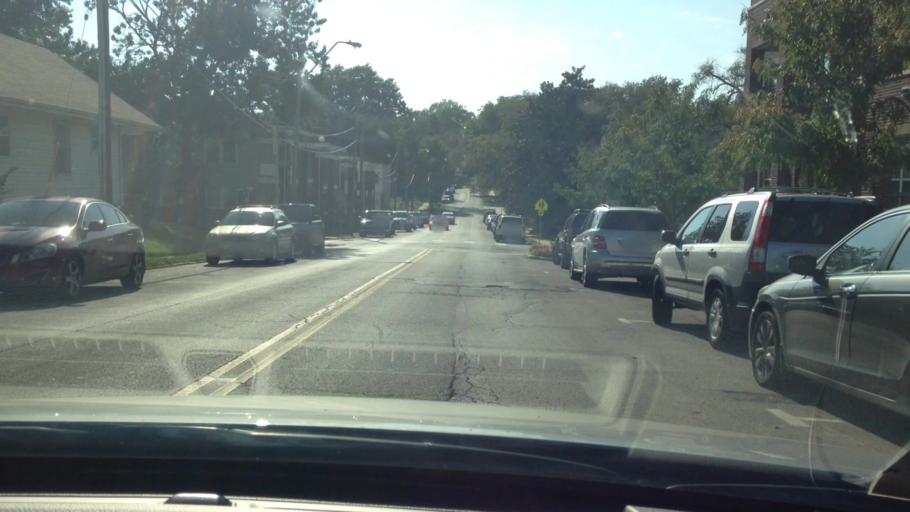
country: US
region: Kansas
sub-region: Johnson County
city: Westwood
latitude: 39.0348
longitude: -94.5881
